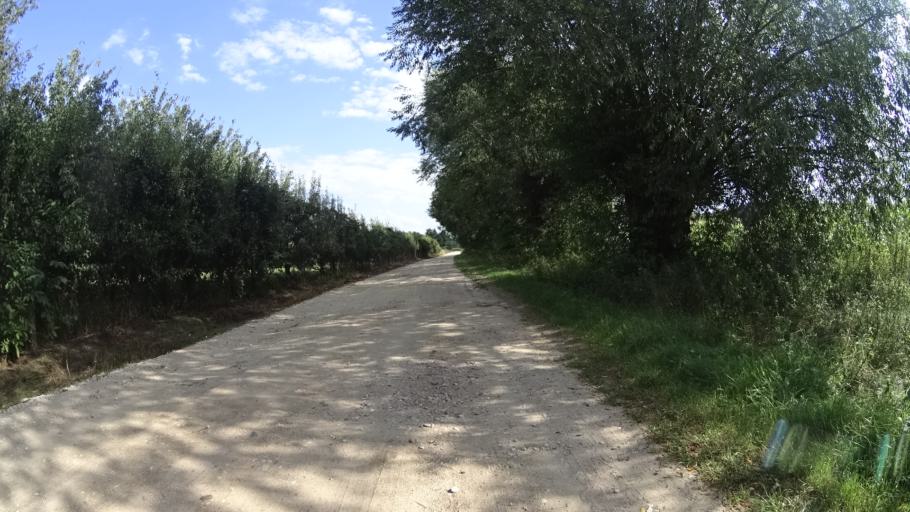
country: PL
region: Masovian Voivodeship
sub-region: Powiat grojecki
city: Mogielnica
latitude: 51.6810
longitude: 20.7631
